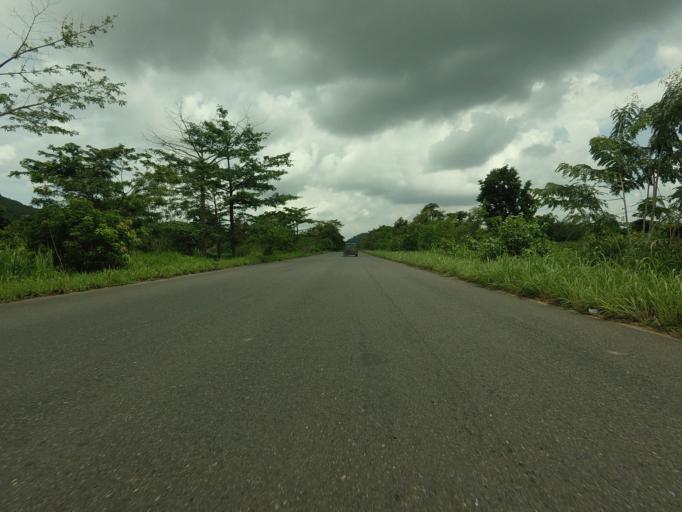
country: GH
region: Volta
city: Ho
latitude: 6.4415
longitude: 0.1731
